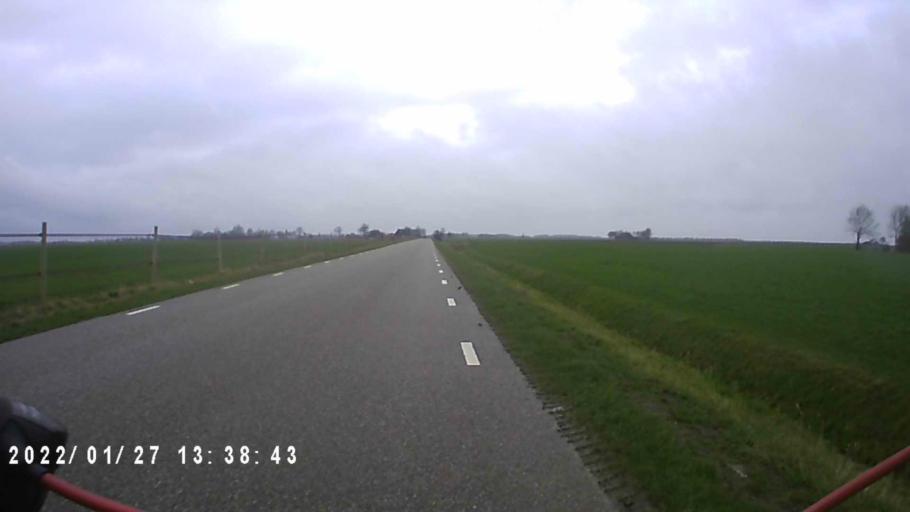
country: NL
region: Friesland
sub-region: Gemeente Kollumerland en Nieuwkruisland
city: Kollum
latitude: 53.2971
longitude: 6.2221
